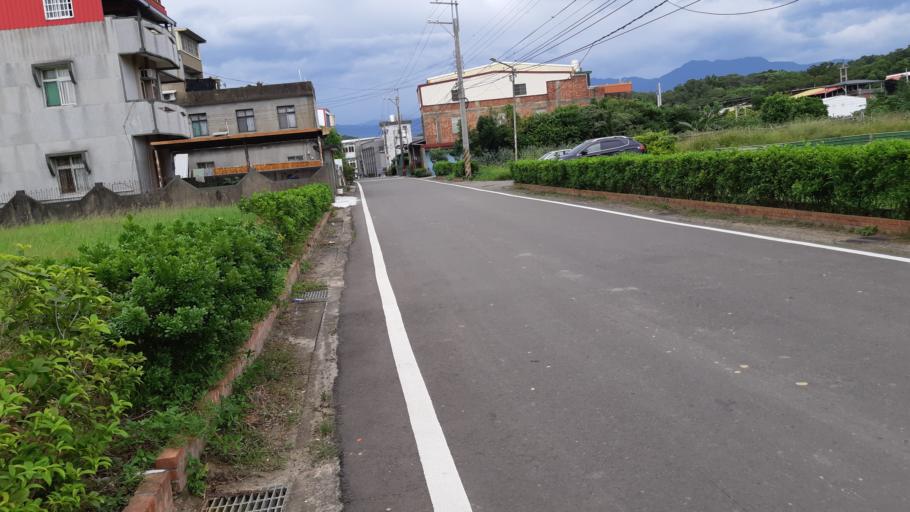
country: TW
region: Taiwan
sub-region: Miaoli
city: Miaoli
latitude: 24.6590
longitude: 120.8854
